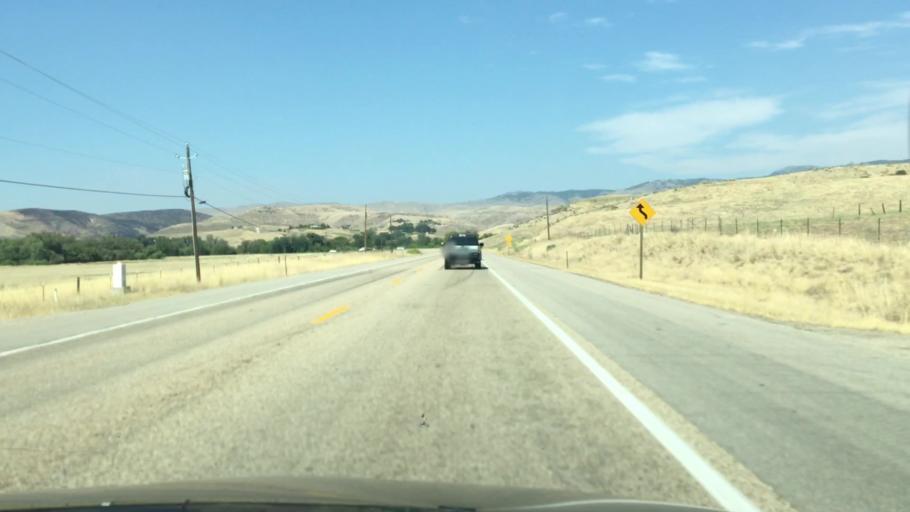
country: US
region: Idaho
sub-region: Ada County
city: Eagle
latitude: 43.7270
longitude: -116.3091
